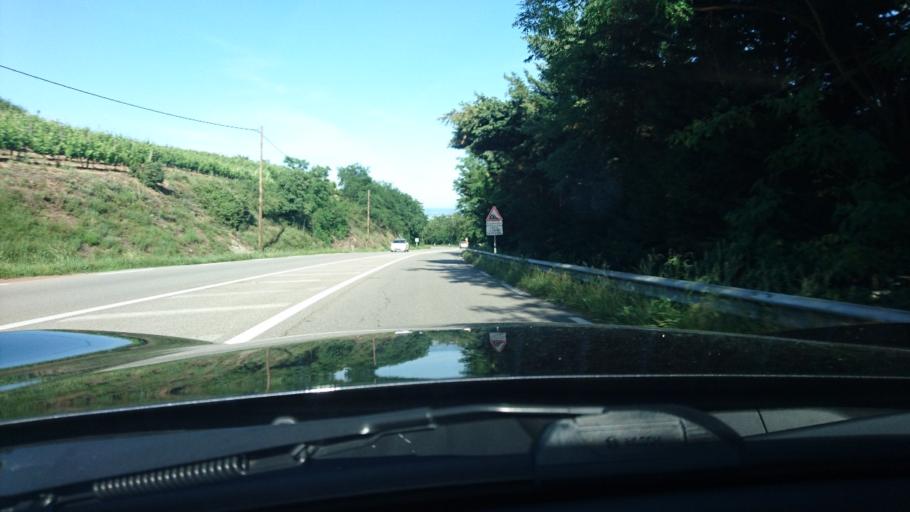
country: FR
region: Rhone-Alpes
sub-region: Departement de l'Ardeche
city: Serrieres
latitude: 45.3099
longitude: 4.7487
